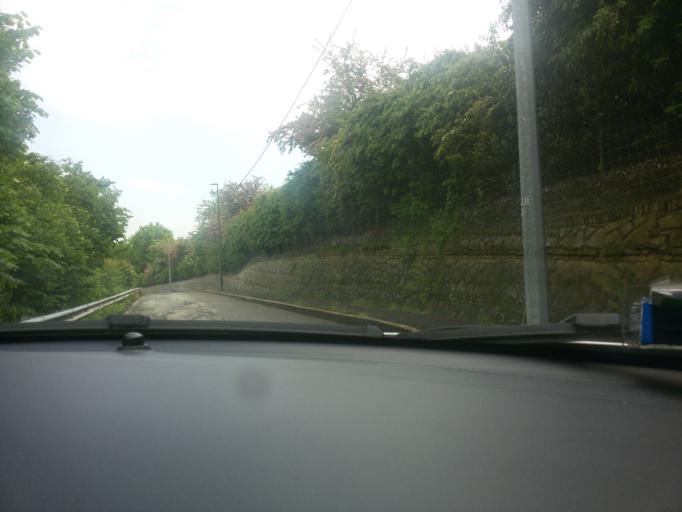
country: IT
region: Piedmont
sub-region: Provincia di Torino
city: Turin
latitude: 45.0469
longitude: 7.7020
